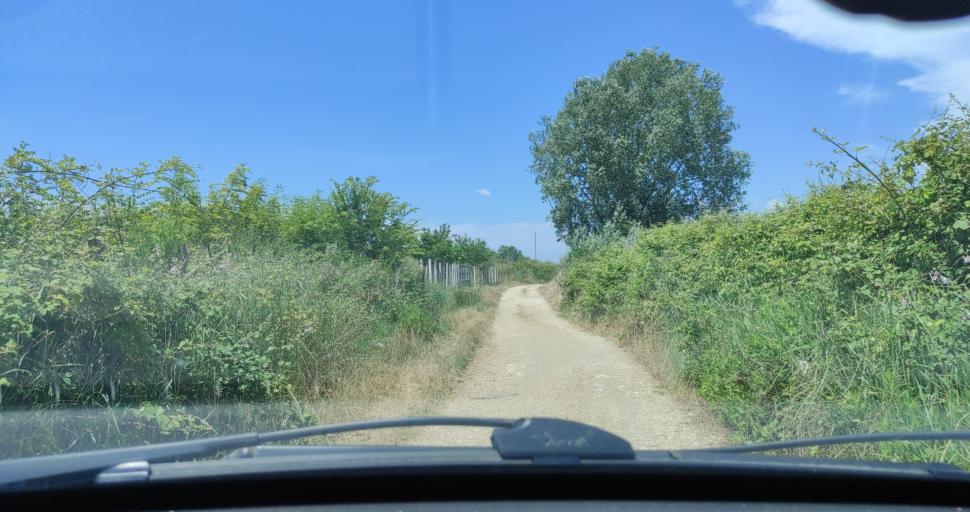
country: AL
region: Shkoder
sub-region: Rrethi i Shkodres
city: Velipoje
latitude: 41.8836
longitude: 19.3895
